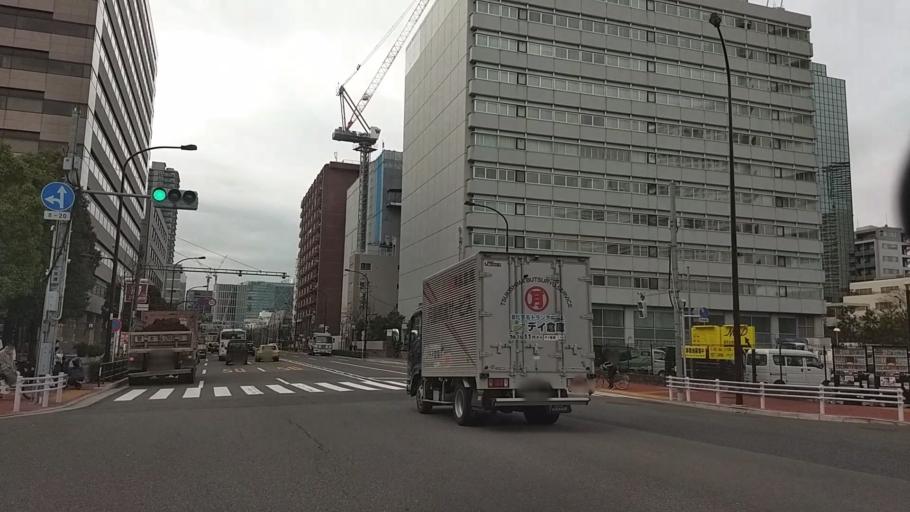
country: JP
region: Tokyo
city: Tokyo
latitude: 35.6413
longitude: 139.7481
